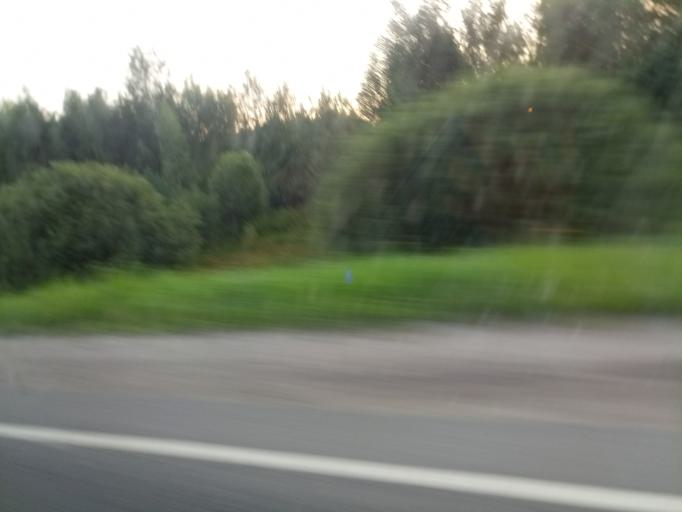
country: RU
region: Moskovskaya
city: Noginsk-9
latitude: 56.0611
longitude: 38.5537
